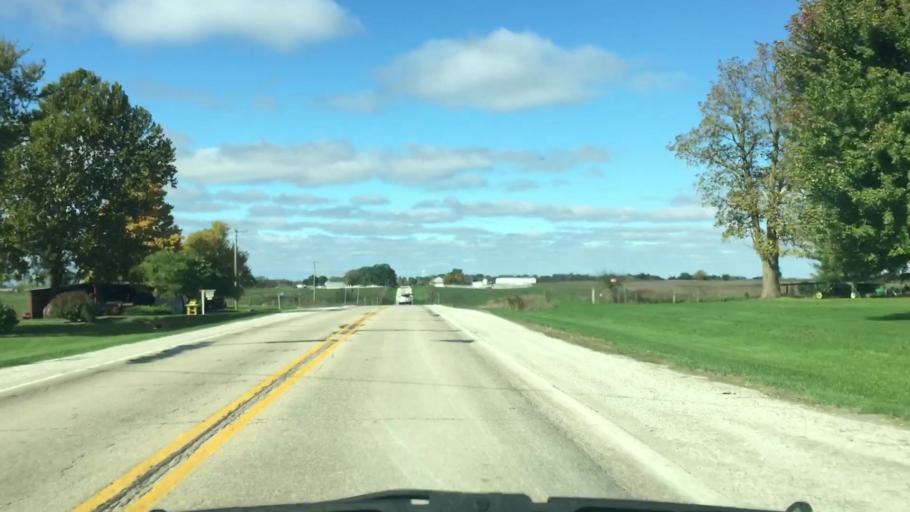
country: US
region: Iowa
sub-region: Decatur County
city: Leon
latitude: 40.7420
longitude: -93.8039
